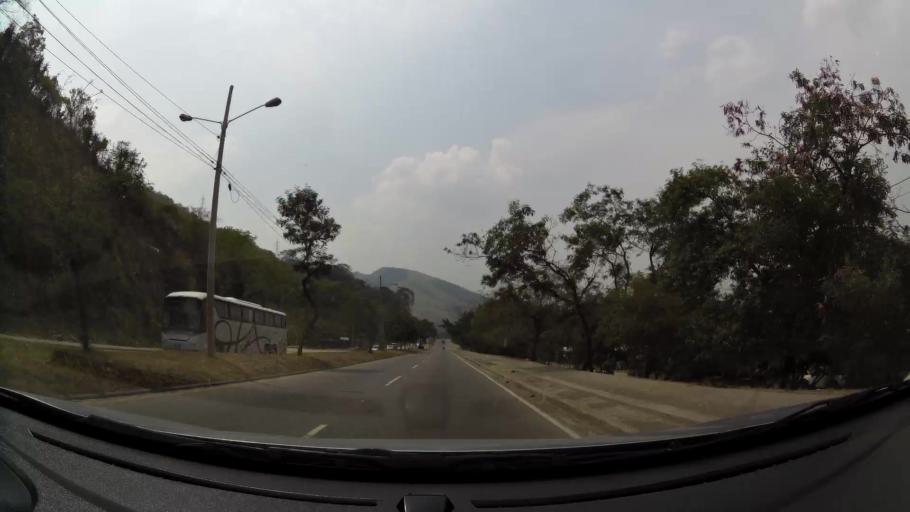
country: HN
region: Cortes
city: Chotepe
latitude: 15.4187
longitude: -88.0173
